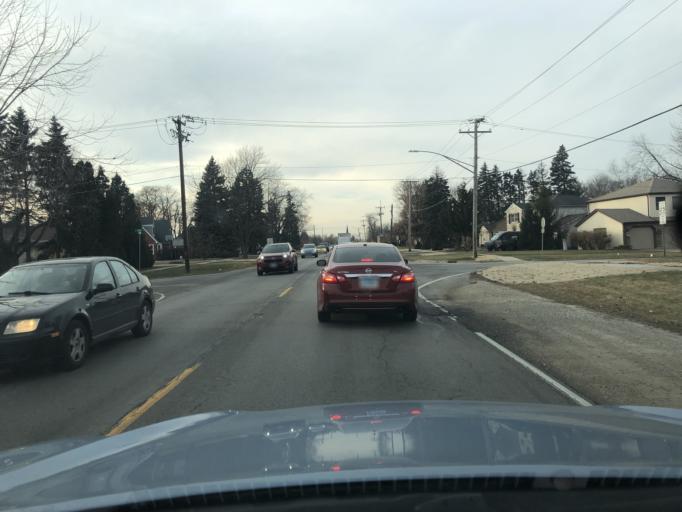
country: US
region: Illinois
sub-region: DuPage County
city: Itasca
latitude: 41.9678
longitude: -88.0053
